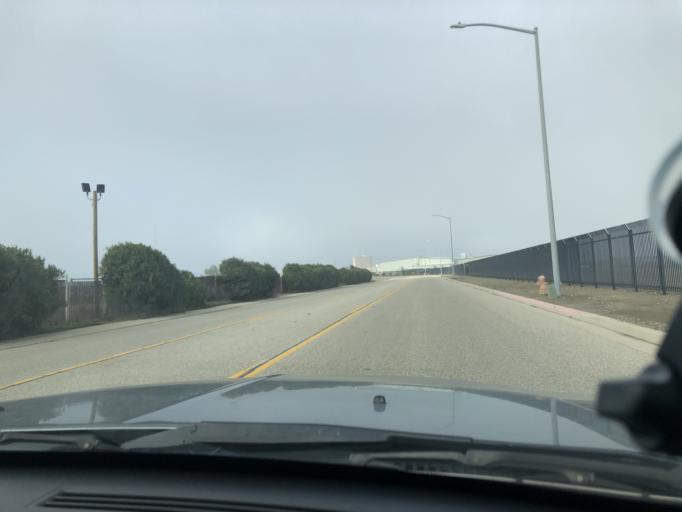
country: US
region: California
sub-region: Monterey County
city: King City
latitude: 36.2260
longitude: -121.1209
